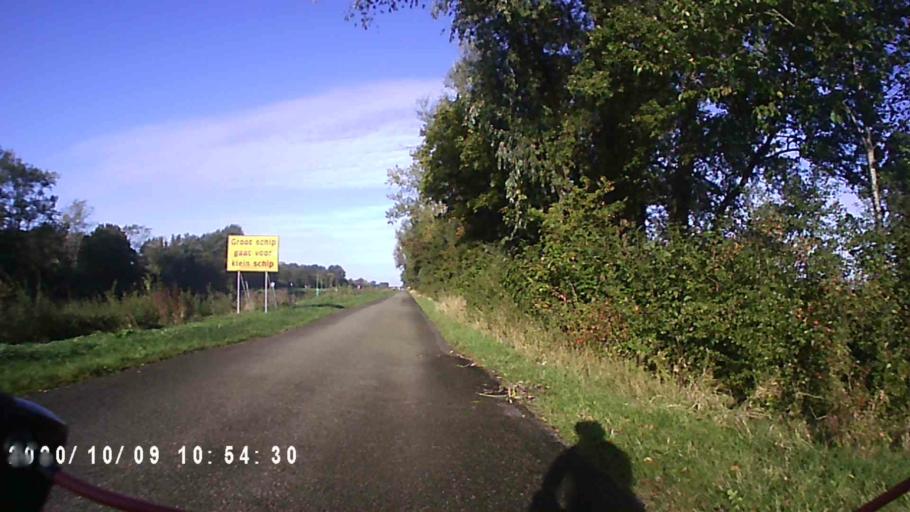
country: NL
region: Groningen
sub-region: Gemeente Groningen
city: Korrewegwijk
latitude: 53.2488
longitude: 6.5376
